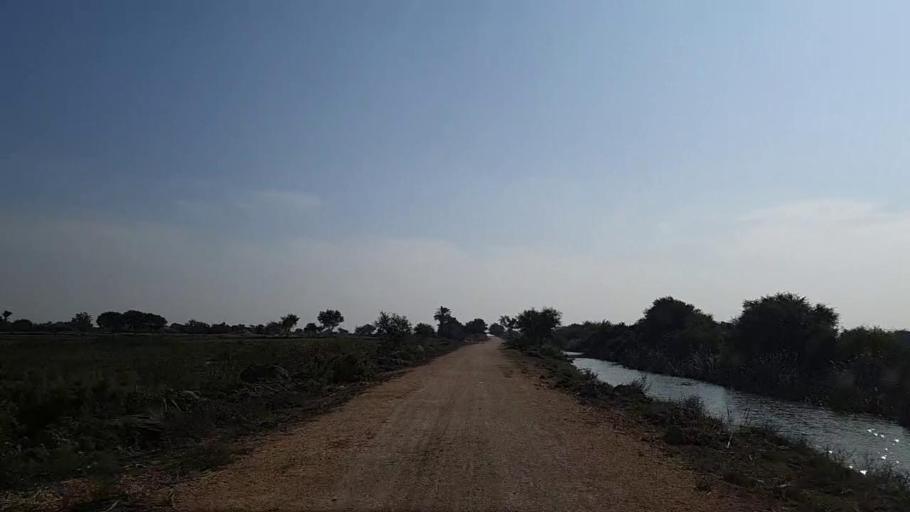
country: PK
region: Sindh
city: Daro Mehar
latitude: 24.7215
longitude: 68.1157
